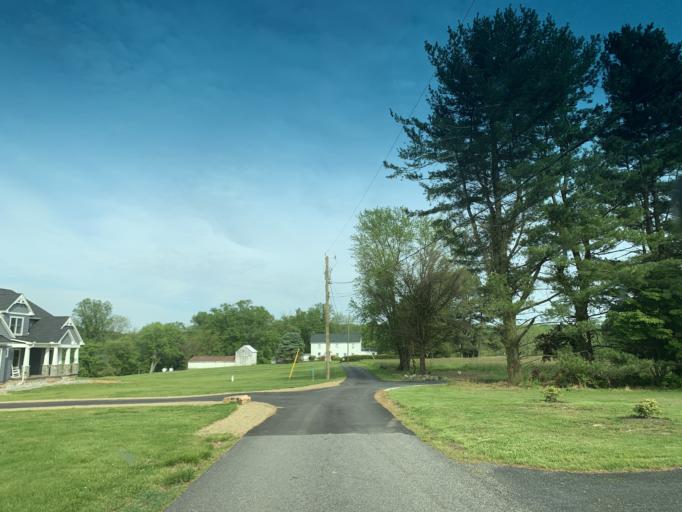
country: US
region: Maryland
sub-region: Baltimore County
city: Perry Hall
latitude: 39.4513
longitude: -76.4595
